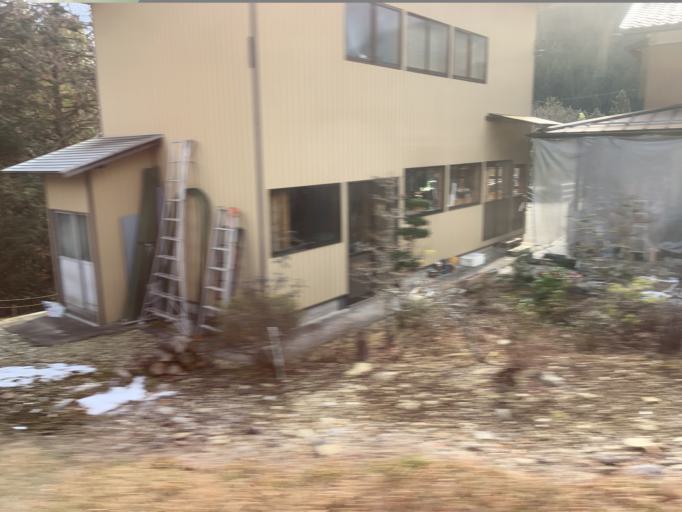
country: JP
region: Gifu
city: Takayama
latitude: 35.9275
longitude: 137.2087
